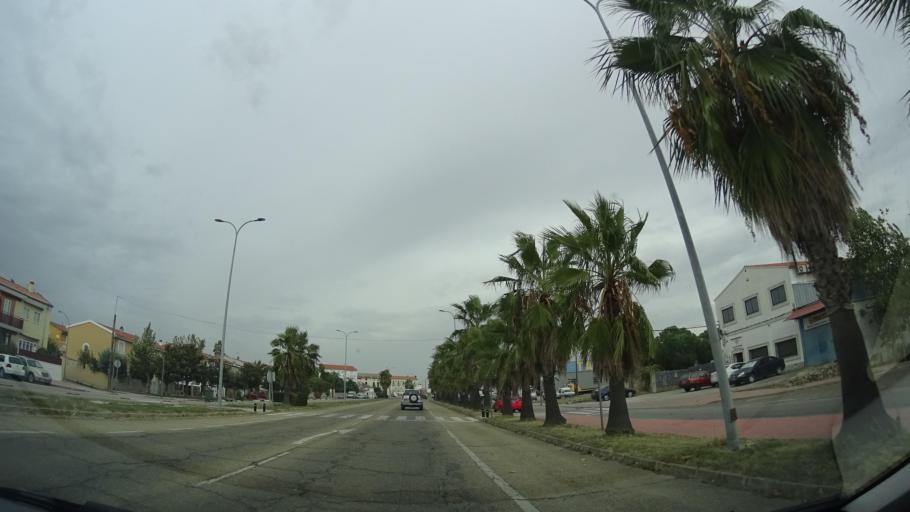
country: ES
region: Extremadura
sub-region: Provincia de Caceres
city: Trujillo
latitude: 39.4563
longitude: -5.8765
